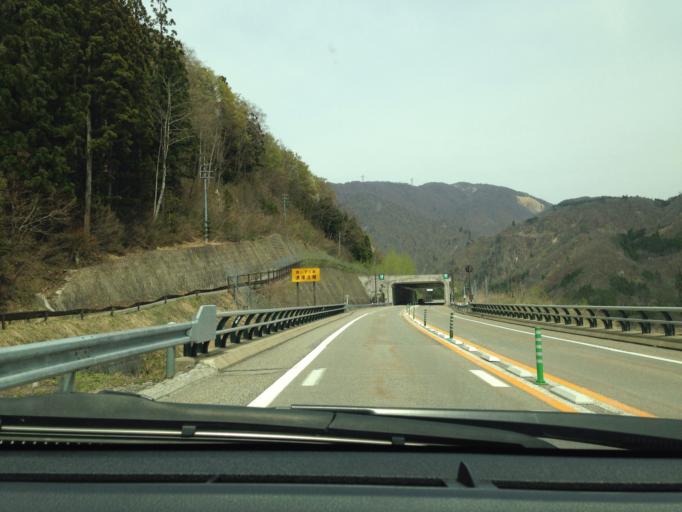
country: JP
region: Toyama
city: Fukumitsu
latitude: 36.2787
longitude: 136.8966
